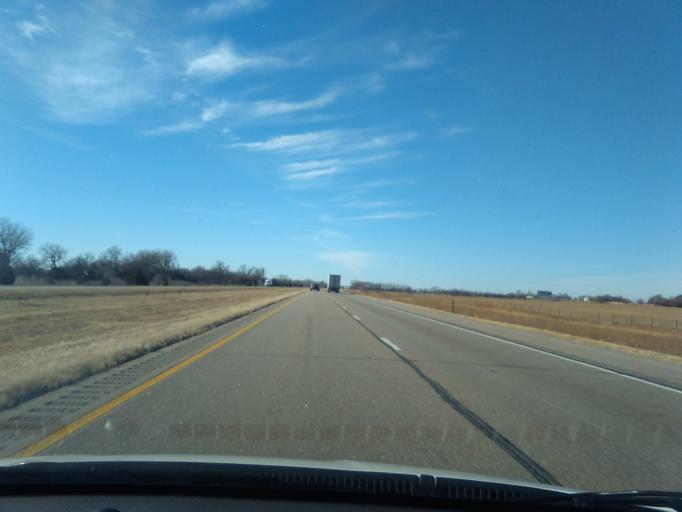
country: US
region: Nebraska
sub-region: Hall County
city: Grand Island
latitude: 40.8141
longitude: -98.4366
